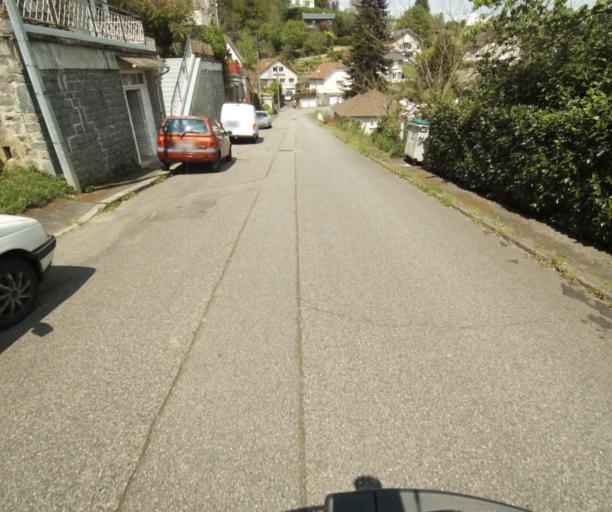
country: FR
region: Limousin
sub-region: Departement de la Correze
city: Tulle
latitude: 45.2696
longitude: 1.7649
